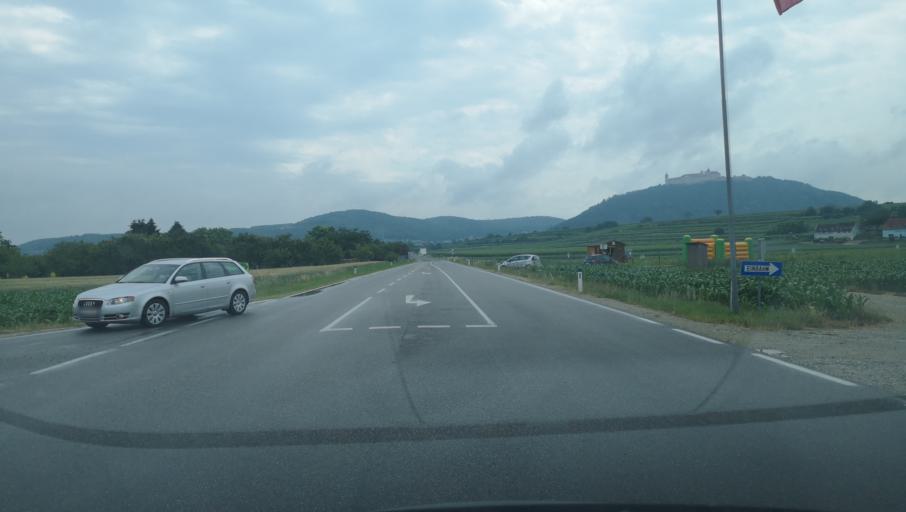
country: AT
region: Lower Austria
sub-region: Politischer Bezirk Krems
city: Weinzierl bei Krems
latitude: 48.3865
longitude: 15.5971
